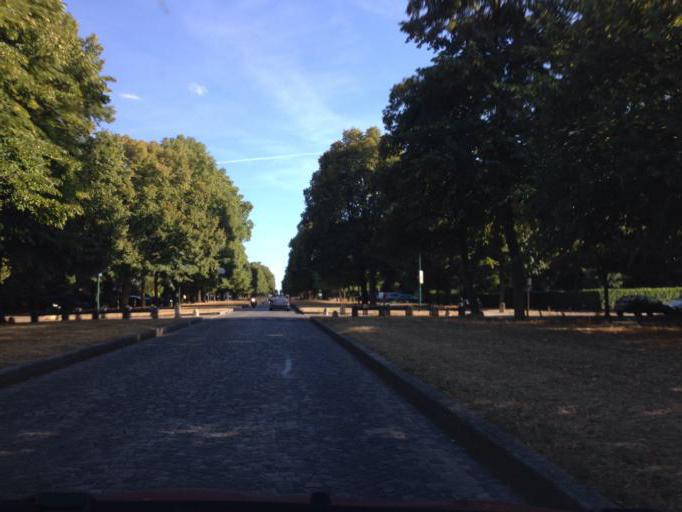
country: FR
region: Ile-de-France
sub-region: Departement des Hauts-de-Seine
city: Meudon
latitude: 48.8165
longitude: 2.2301
